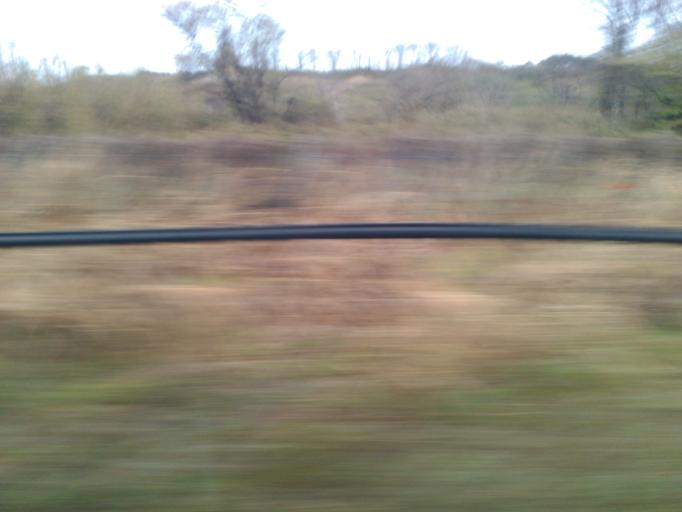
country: JP
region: Miyagi
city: Tomiya
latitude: 38.4160
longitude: 140.9635
